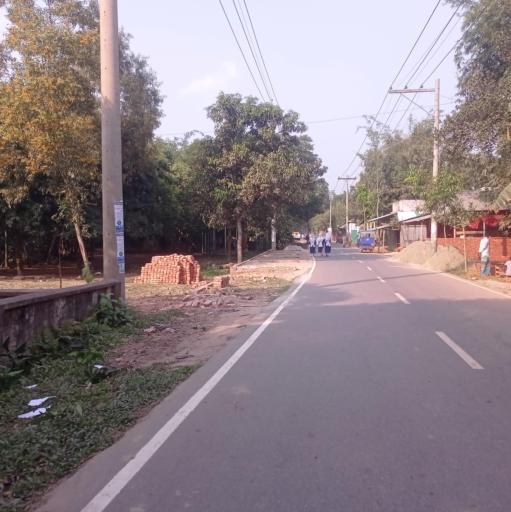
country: BD
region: Dhaka
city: Bhairab Bazar
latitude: 24.0649
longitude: 90.8413
